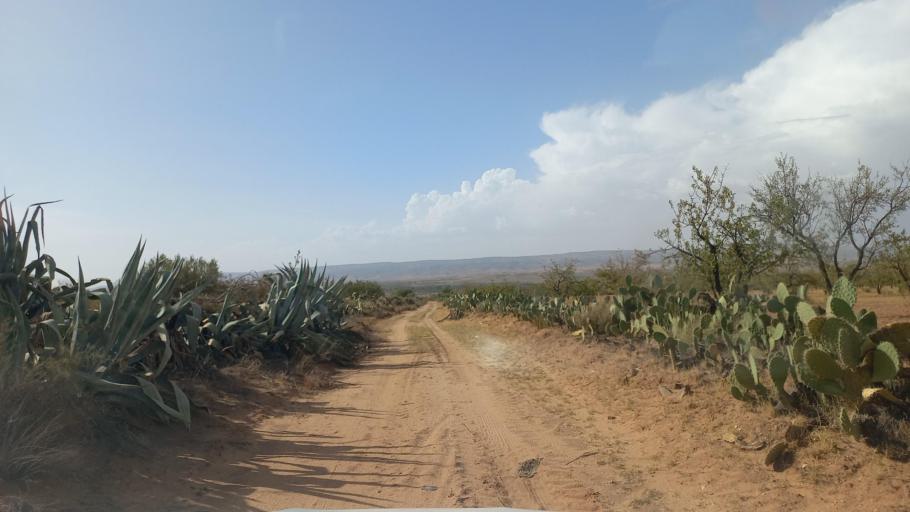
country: TN
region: Al Qasrayn
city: Kasserine
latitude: 35.2077
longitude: 8.9578
